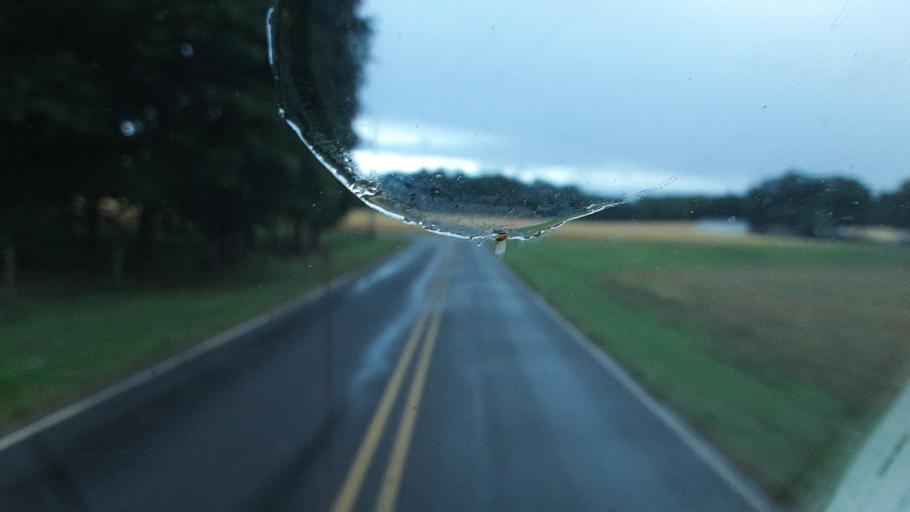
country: US
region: North Carolina
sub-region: Yadkin County
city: Jonesville
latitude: 36.0951
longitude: -80.8656
